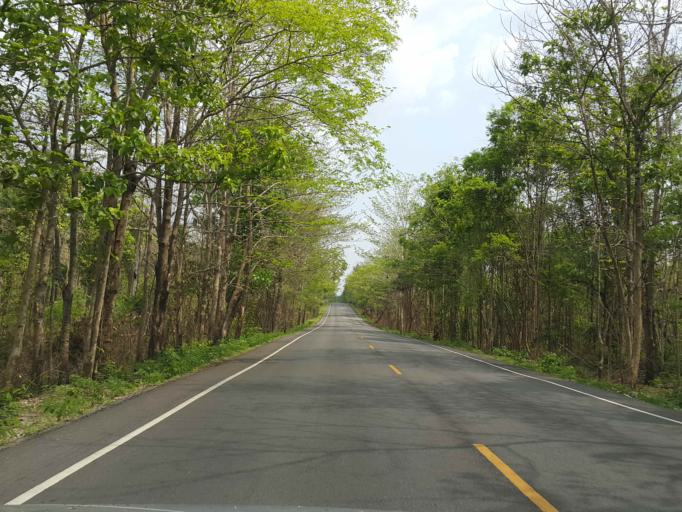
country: TH
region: Sukhothai
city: Thung Saliam
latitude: 17.4275
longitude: 99.3774
